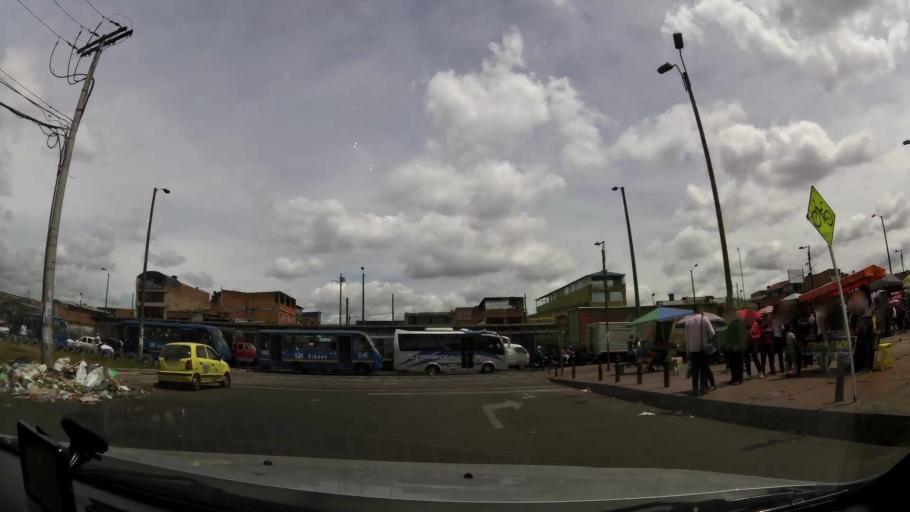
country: CO
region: Cundinamarca
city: Soacha
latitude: 4.6372
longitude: -74.1606
